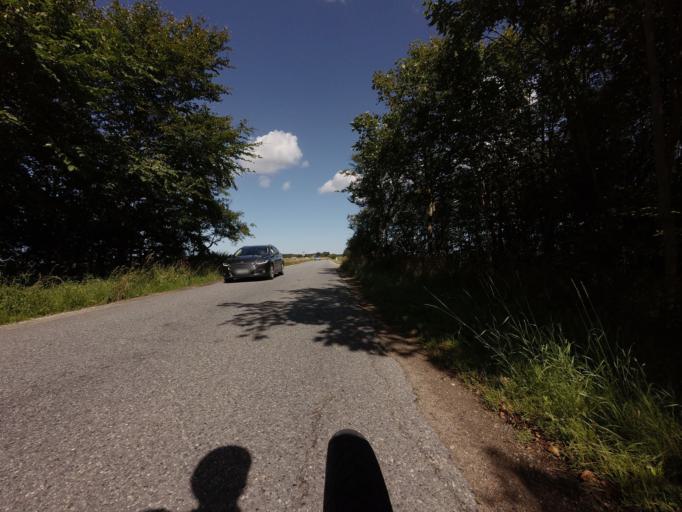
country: DK
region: North Denmark
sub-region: Hjorring Kommune
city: Hjorring
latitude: 57.4791
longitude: 9.9030
